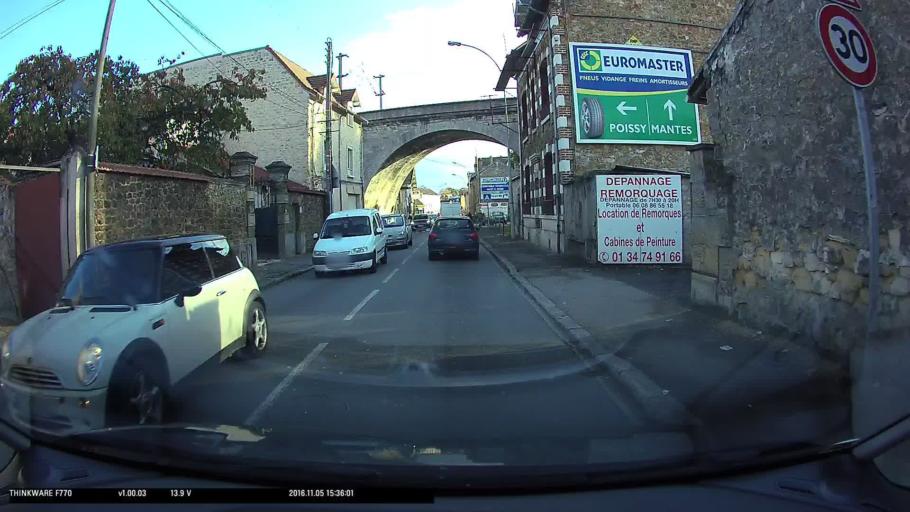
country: FR
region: Ile-de-France
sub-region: Departement des Yvelines
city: Meulan-en-Yvelines
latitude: 49.0068
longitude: 1.9057
